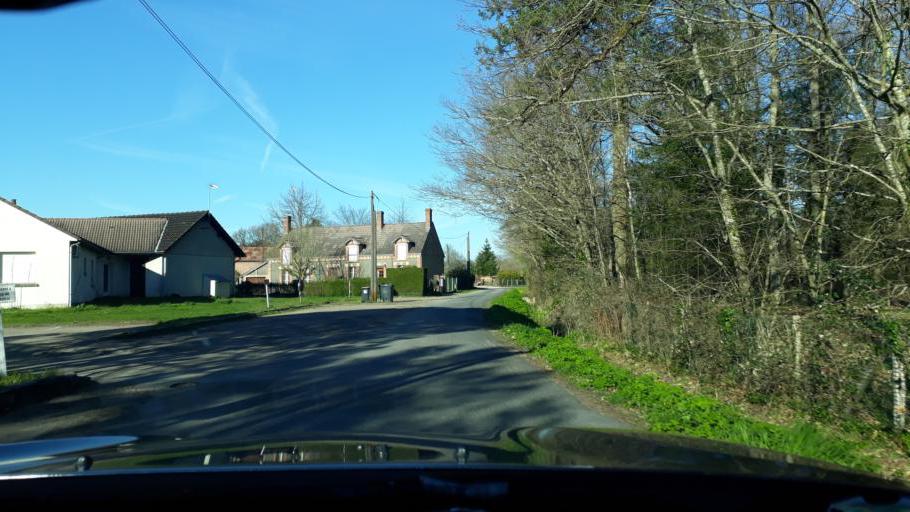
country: FR
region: Centre
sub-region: Departement du Loiret
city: Ligny-le-Ribault
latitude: 47.6869
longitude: 1.7842
